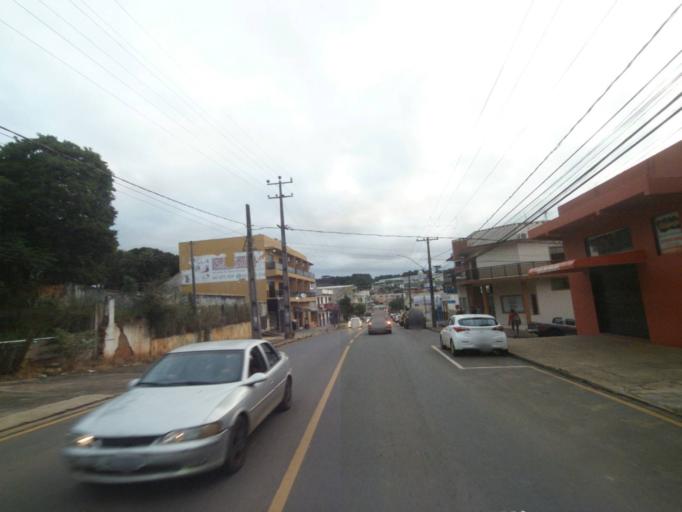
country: BR
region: Parana
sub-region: Telemaco Borba
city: Telemaco Borba
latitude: -24.3325
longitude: -50.6354
